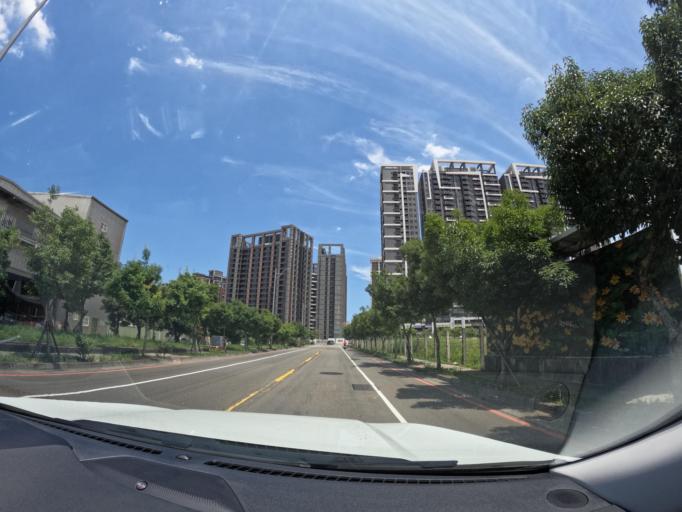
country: TW
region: Taiwan
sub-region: Taoyuan
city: Taoyuan
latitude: 25.0455
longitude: 121.3839
